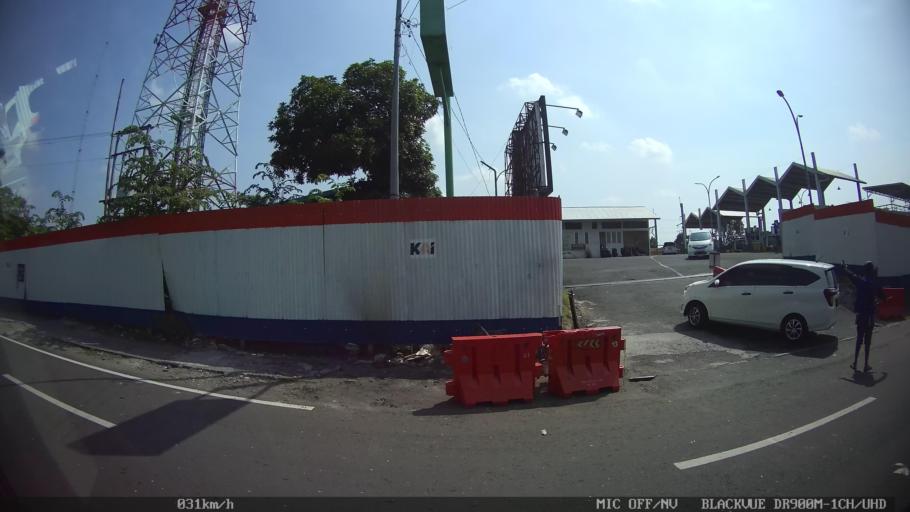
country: ID
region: Daerah Istimewa Yogyakarta
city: Yogyakarta
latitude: -7.7897
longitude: 110.3600
